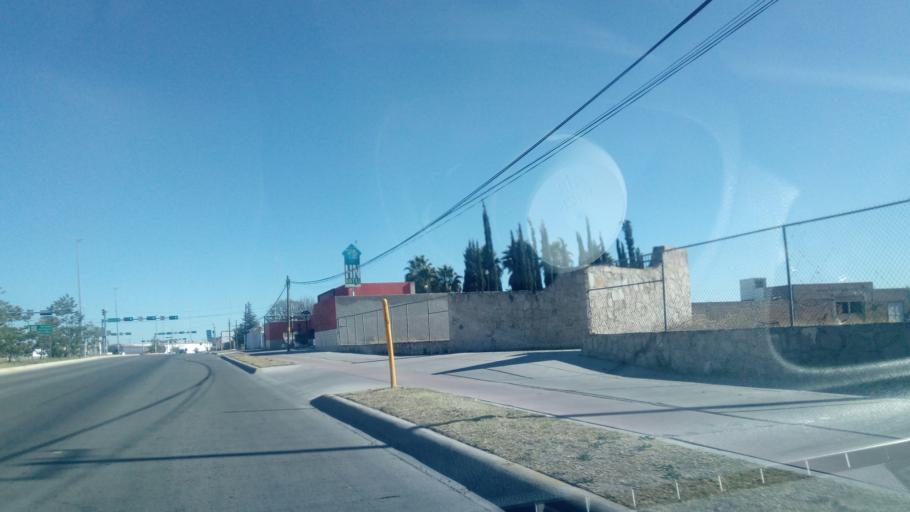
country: MX
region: Durango
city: Victoria de Durango
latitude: 24.0894
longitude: -104.5801
